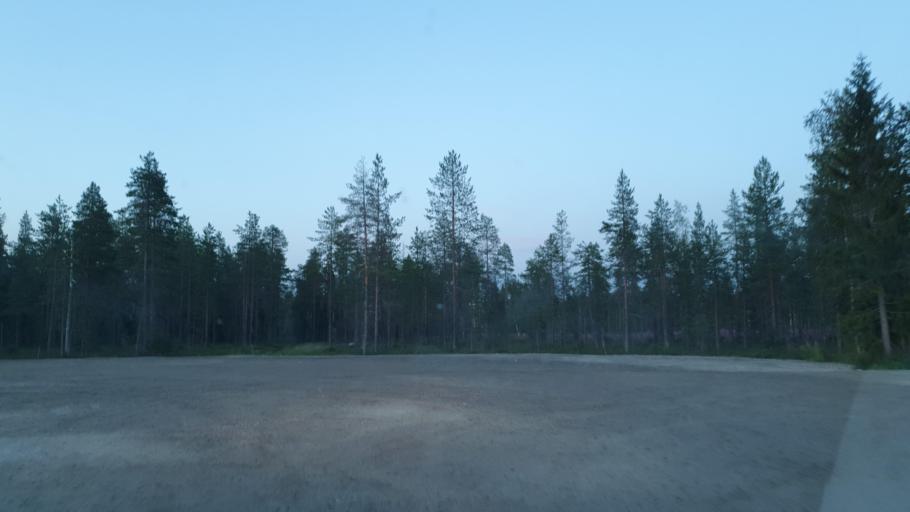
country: FI
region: Kainuu
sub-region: Kehys-Kainuu
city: Suomussalmi
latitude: 65.0938
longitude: 28.9038
